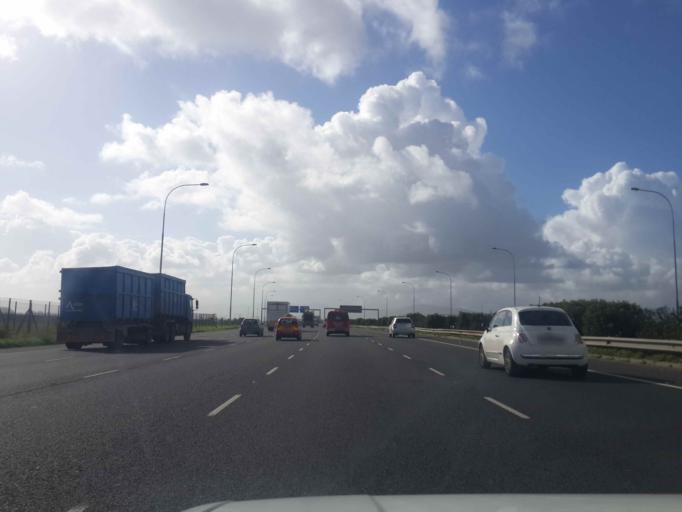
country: ZA
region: Western Cape
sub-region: City of Cape Town
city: Rosebank
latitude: -33.9142
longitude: 18.4940
